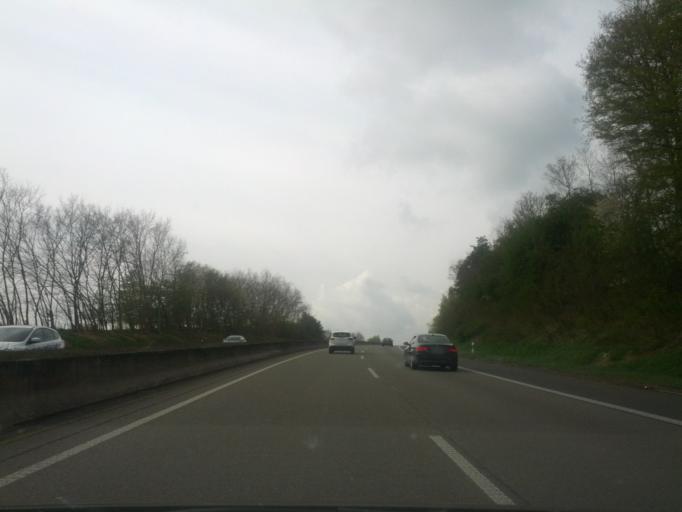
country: DE
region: Thuringia
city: Gerstungen
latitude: 50.9726
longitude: 10.0684
